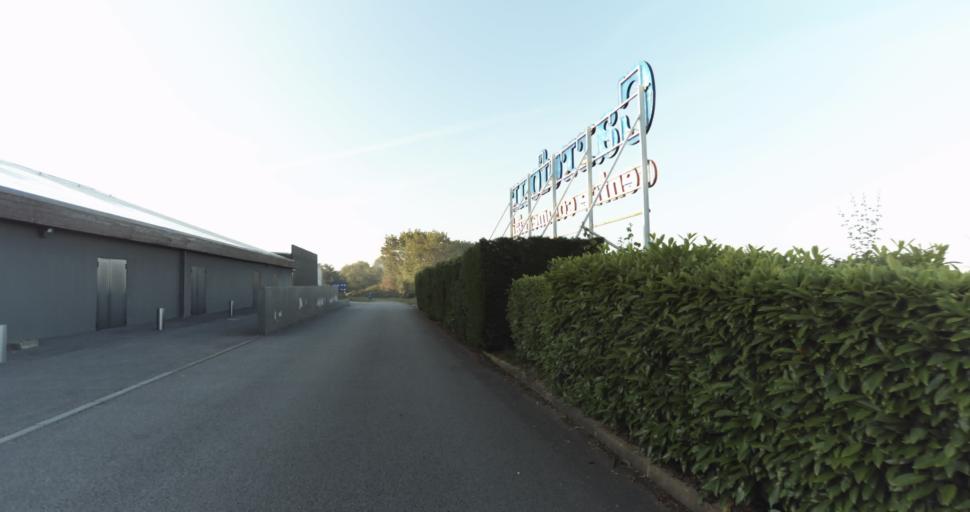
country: FR
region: Limousin
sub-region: Departement de la Haute-Vienne
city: Condat-sur-Vienne
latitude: 45.7776
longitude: 1.3074
